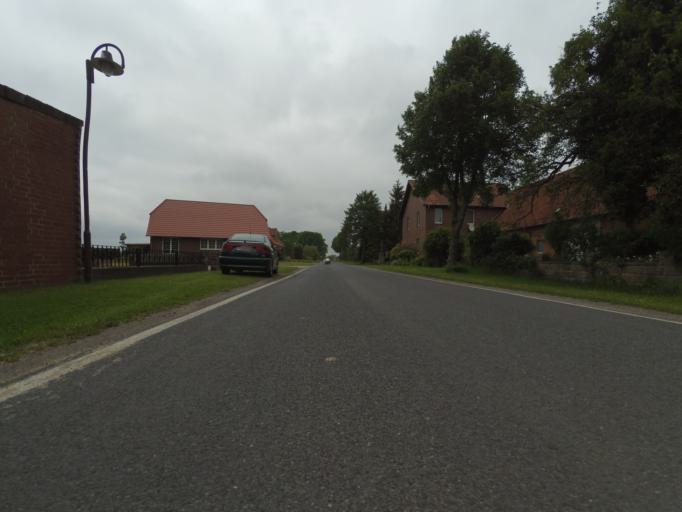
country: DE
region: Lower Saxony
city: Edemissen
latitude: 52.3929
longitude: 10.3214
